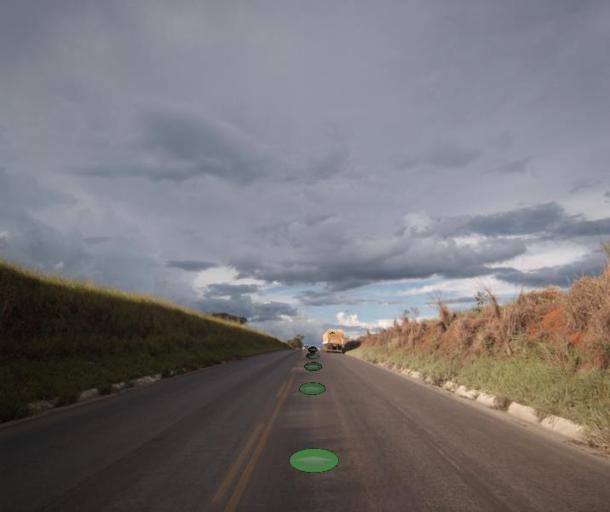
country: BR
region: Goias
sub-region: Itapaci
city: Itapaci
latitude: -15.0998
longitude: -49.4772
